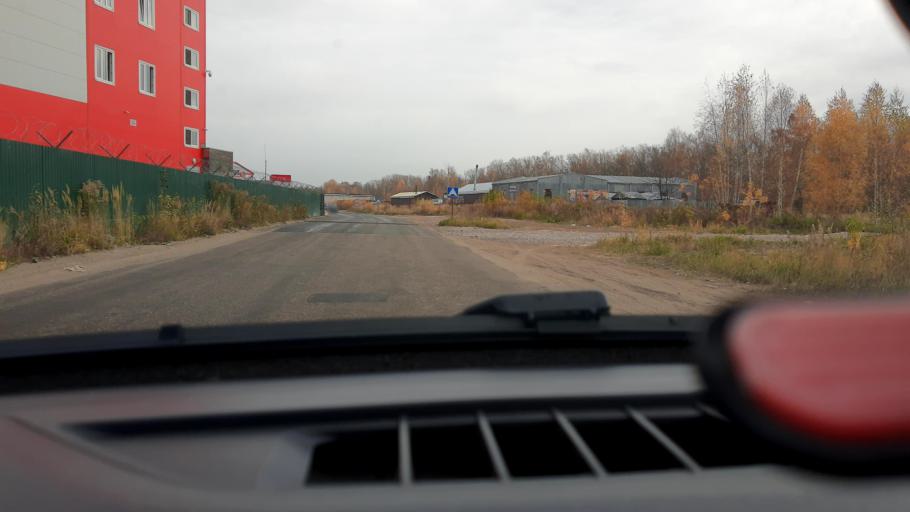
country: RU
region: Nizjnij Novgorod
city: Gorbatovka
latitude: 56.3157
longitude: 43.8507
